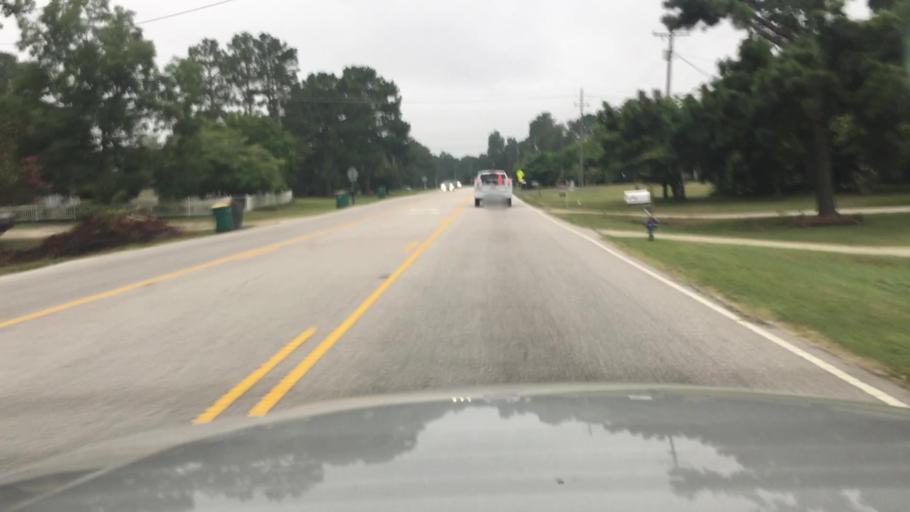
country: US
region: North Carolina
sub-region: Cumberland County
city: Hope Mills
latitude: 34.9781
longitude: -78.9370
